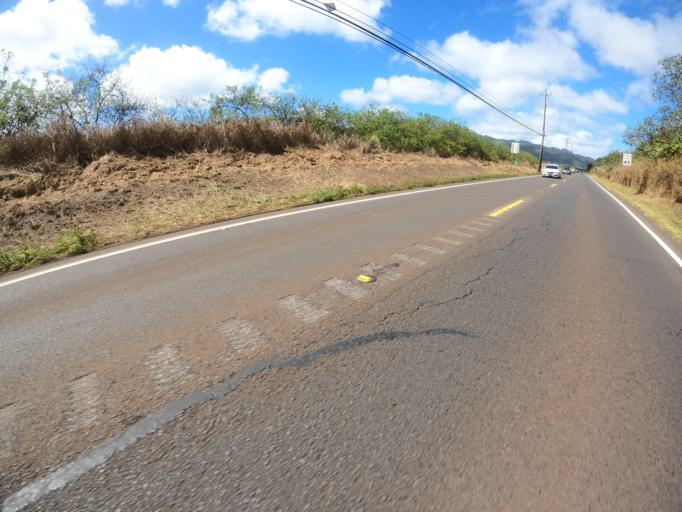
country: US
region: Hawaii
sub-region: Honolulu County
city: Village Park
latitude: 21.4228
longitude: -158.0517
